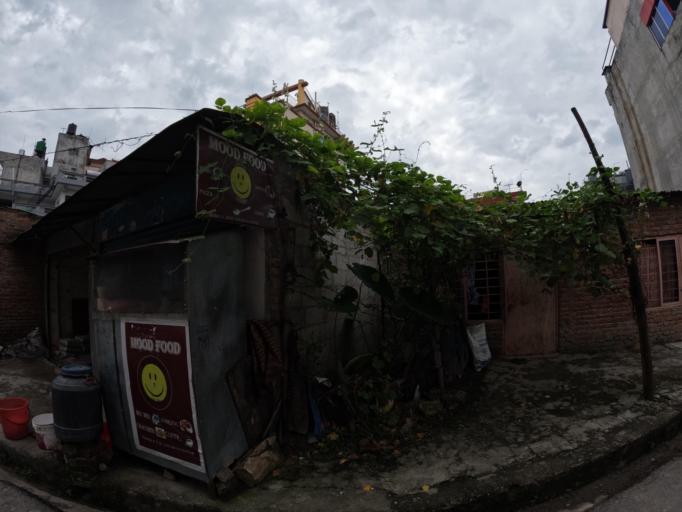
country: NP
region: Central Region
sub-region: Bagmati Zone
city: Kathmandu
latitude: 27.7437
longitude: 85.3196
